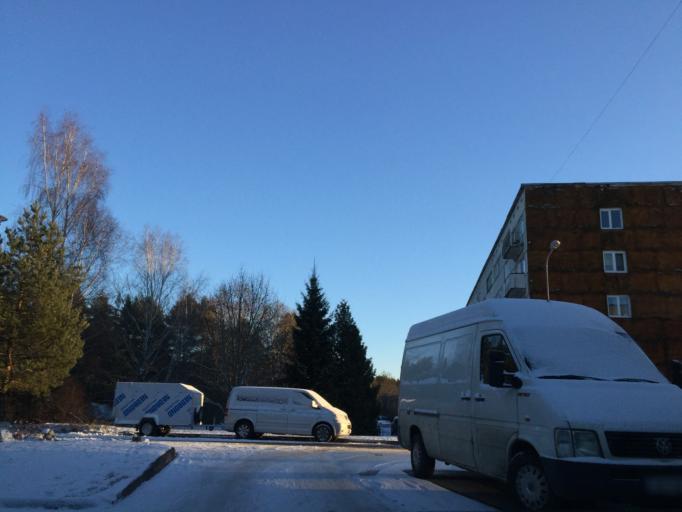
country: LV
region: Kekava
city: Balozi
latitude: 56.8788
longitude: 24.1207
